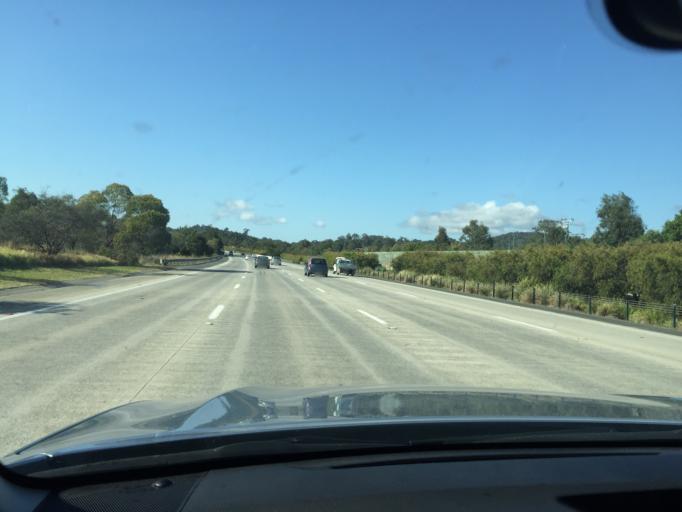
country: AU
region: Queensland
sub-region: Gold Coast
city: Ormeau Hills
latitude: -27.7960
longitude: 153.2608
